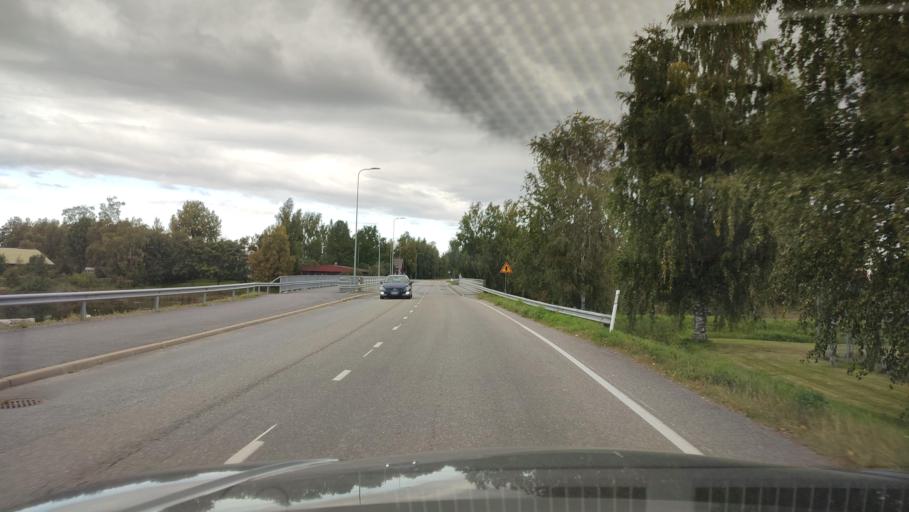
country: FI
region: Ostrobothnia
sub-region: Sydosterbotten
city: Kristinestad
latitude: 62.2553
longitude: 21.5260
